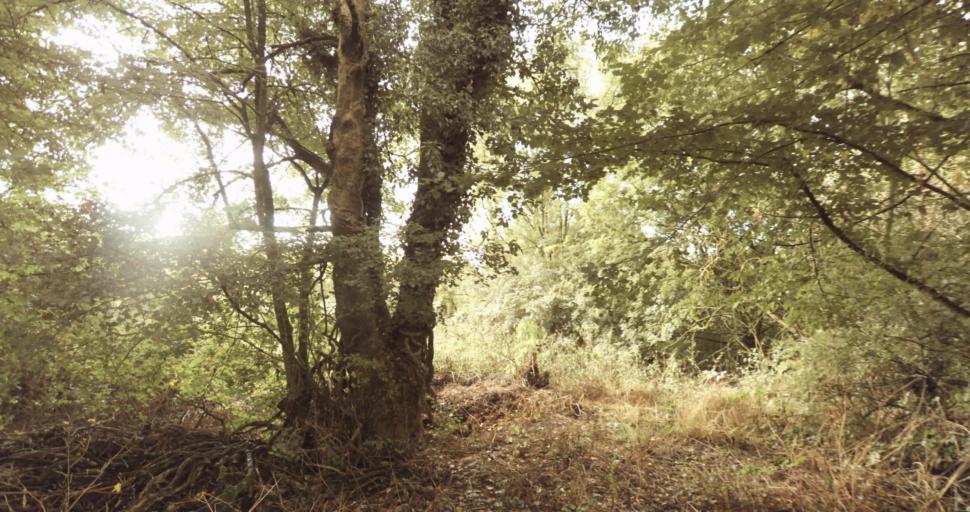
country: FR
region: Lower Normandy
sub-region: Departement de l'Orne
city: Gace
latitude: 48.8444
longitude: 0.3214
